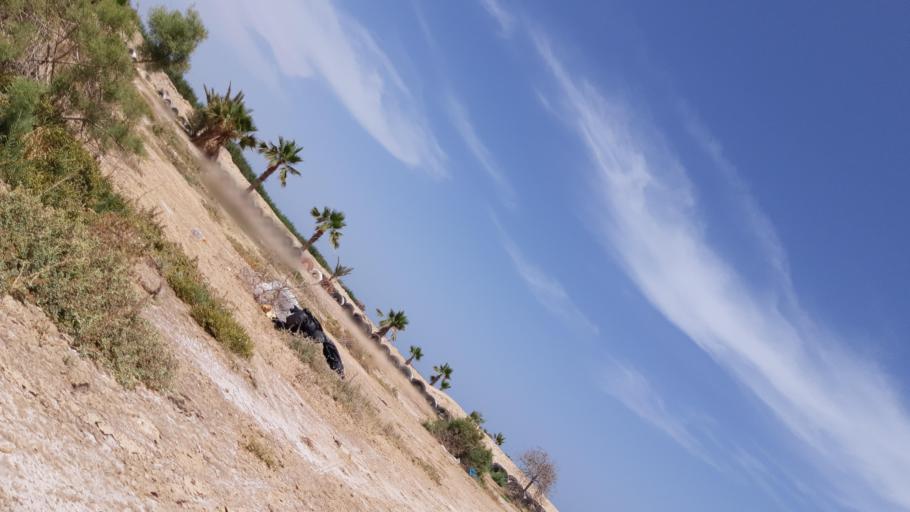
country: TN
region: Qabis
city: Gabes
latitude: 33.8800
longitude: 10.1167
